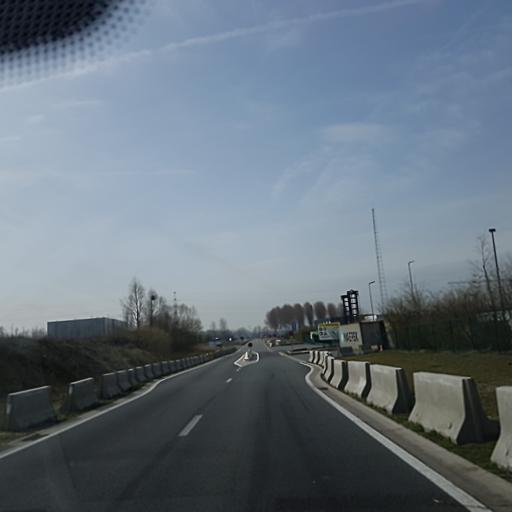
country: BE
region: Flanders
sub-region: Provincie Antwerpen
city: Zwijndrecht
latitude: 51.2412
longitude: 4.3052
